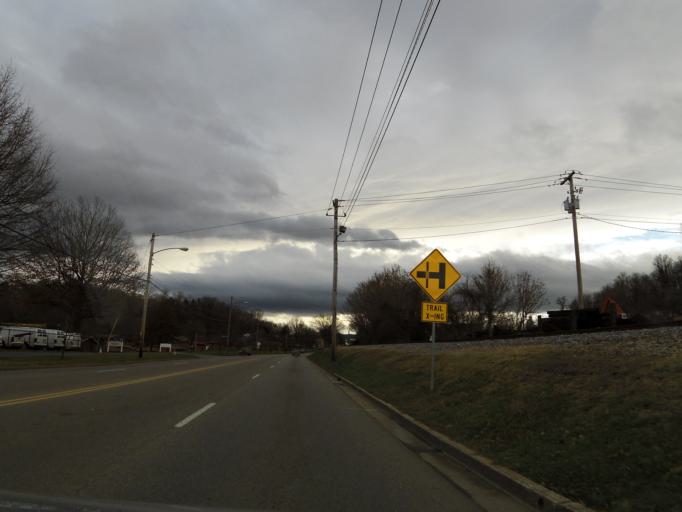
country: US
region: Tennessee
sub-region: Washington County
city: Johnson City
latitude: 36.3172
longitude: -82.3396
